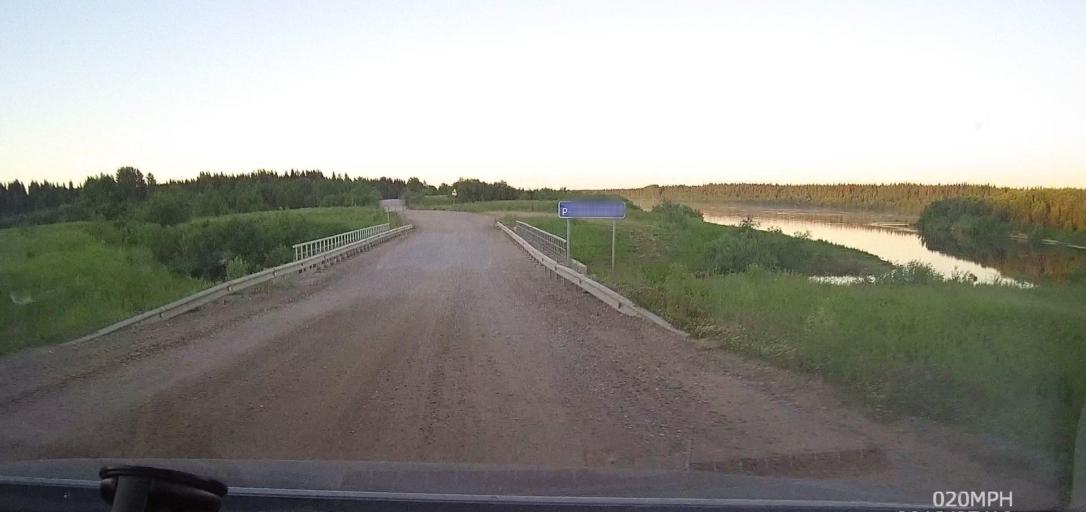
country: RU
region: Arkhangelskaya
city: Lukovetskiy
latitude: 64.2348
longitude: 42.7109
